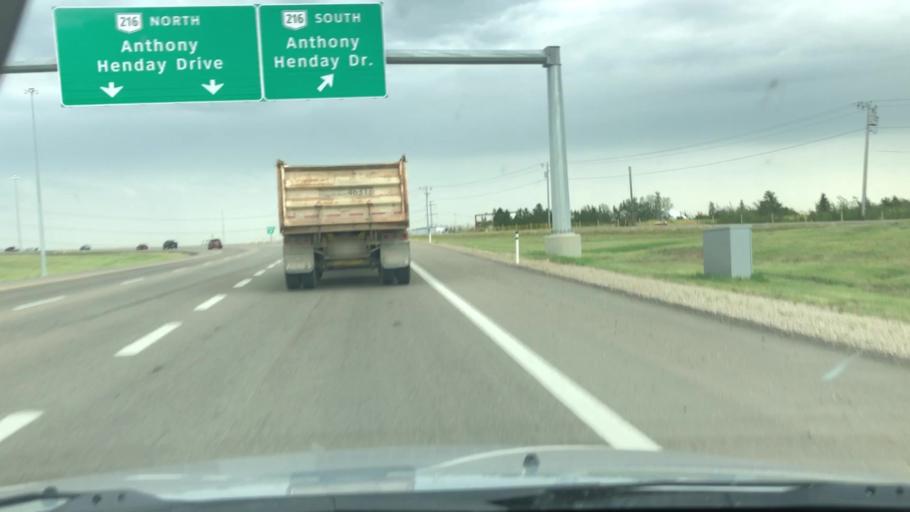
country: CA
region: Alberta
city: Sherwood Park
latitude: 53.5128
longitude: -113.3496
